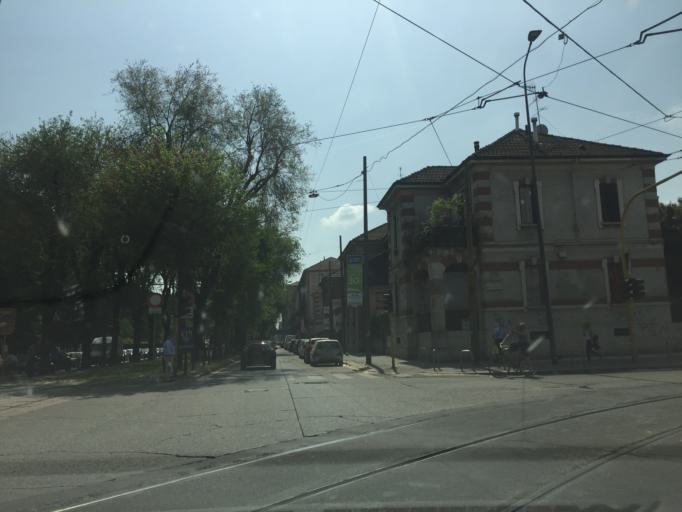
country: IT
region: Lombardy
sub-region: Citta metropolitana di Milano
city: Novate Milanese
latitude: 45.4958
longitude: 9.1553
